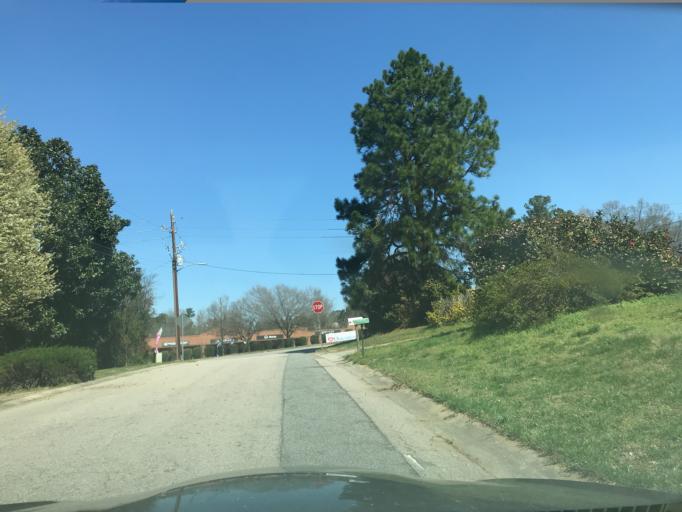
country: US
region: North Carolina
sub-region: Wake County
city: Raleigh
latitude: 35.8477
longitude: -78.5976
